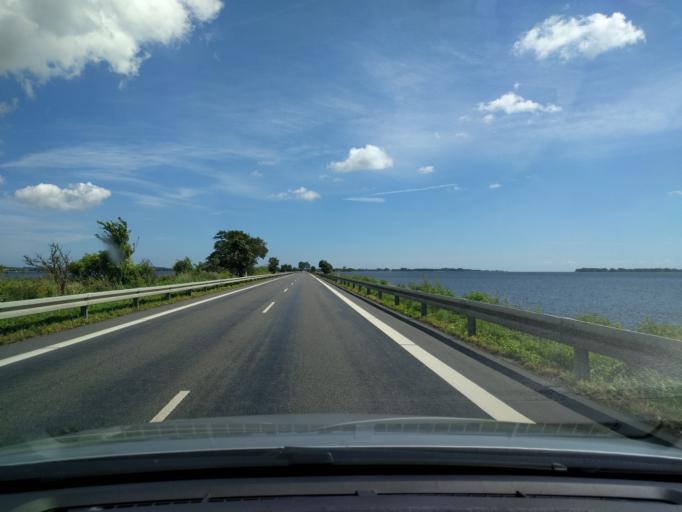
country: DK
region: Zealand
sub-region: Guldborgsund Kommune
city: Stubbekobing
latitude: 54.9086
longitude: 12.0814
